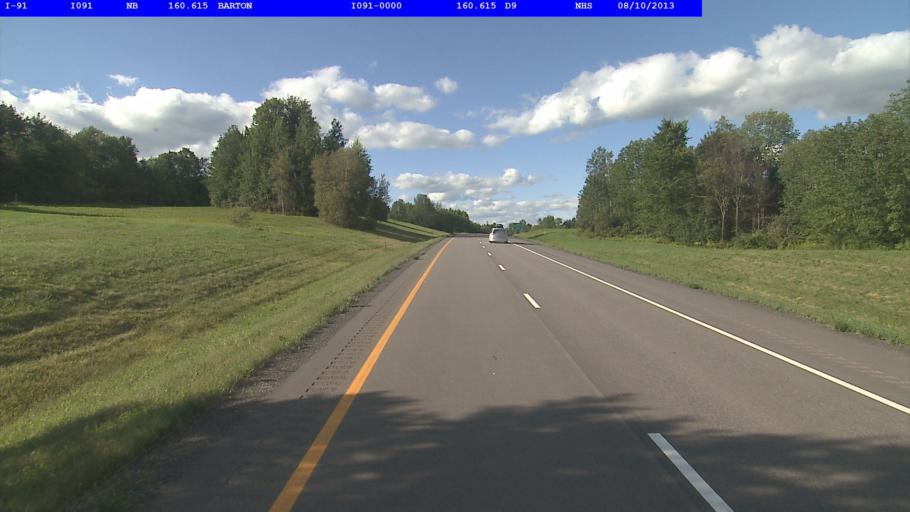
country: US
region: Vermont
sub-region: Orleans County
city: Newport
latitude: 44.7952
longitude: -72.2156
